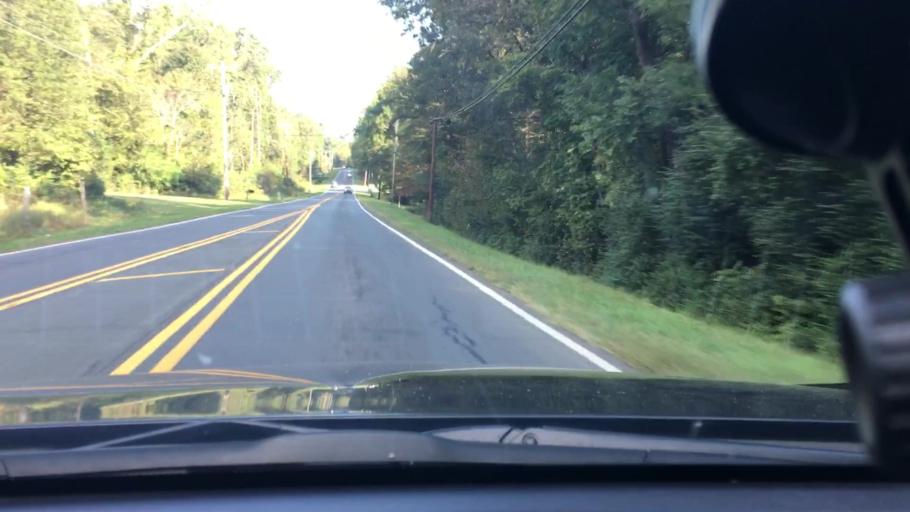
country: US
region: North Carolina
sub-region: Stanly County
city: Albemarle
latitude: 35.3312
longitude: -80.1341
